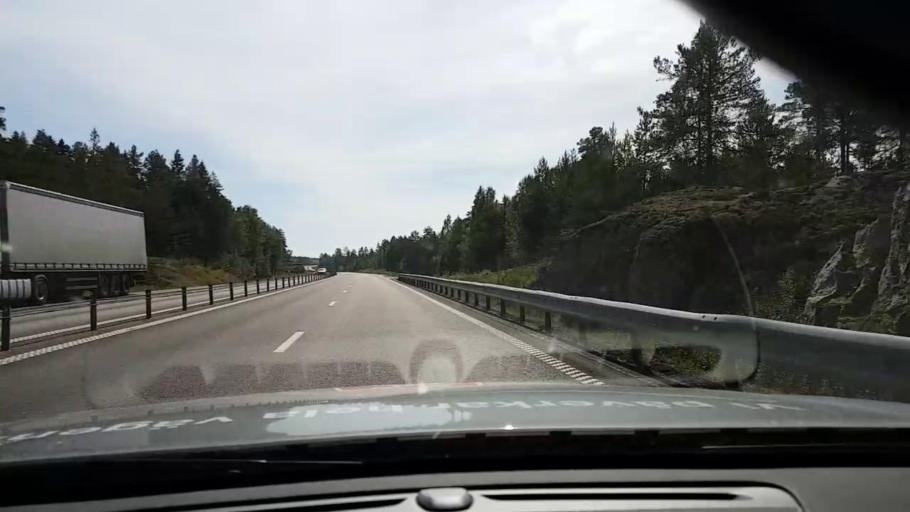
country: SE
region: Vaesternorrland
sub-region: OErnskoeldsviks Kommun
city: Husum
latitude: 63.3812
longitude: 19.1917
